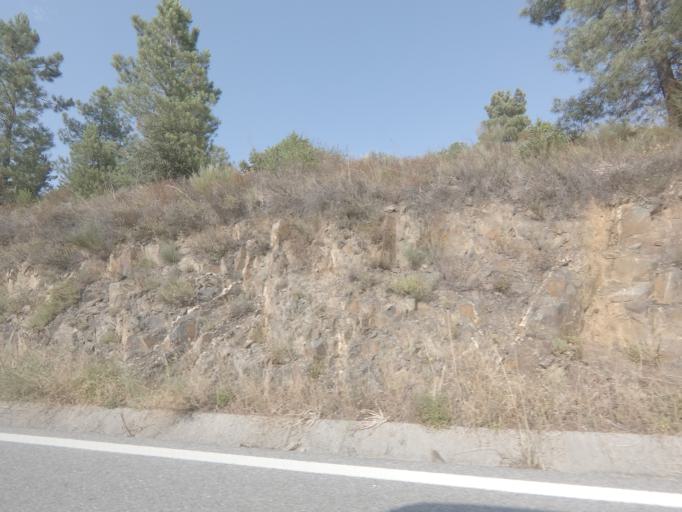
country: PT
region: Viseu
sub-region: Tabuaco
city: Tabuaco
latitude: 41.1441
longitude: -7.5447
